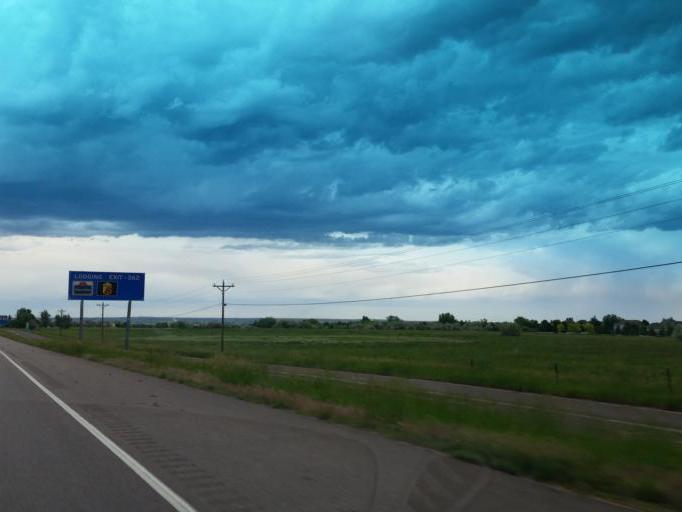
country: US
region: Colorado
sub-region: Weld County
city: Windsor
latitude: 40.4675
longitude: -104.9918
